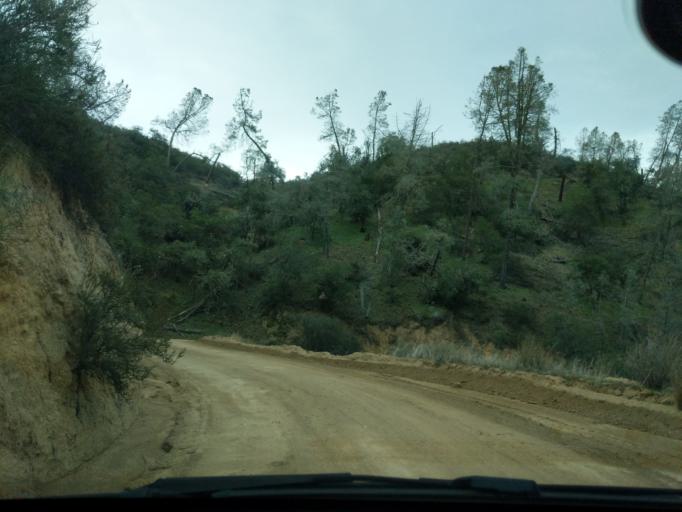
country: US
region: California
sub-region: Monterey County
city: Soledad
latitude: 36.5308
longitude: -121.3028
